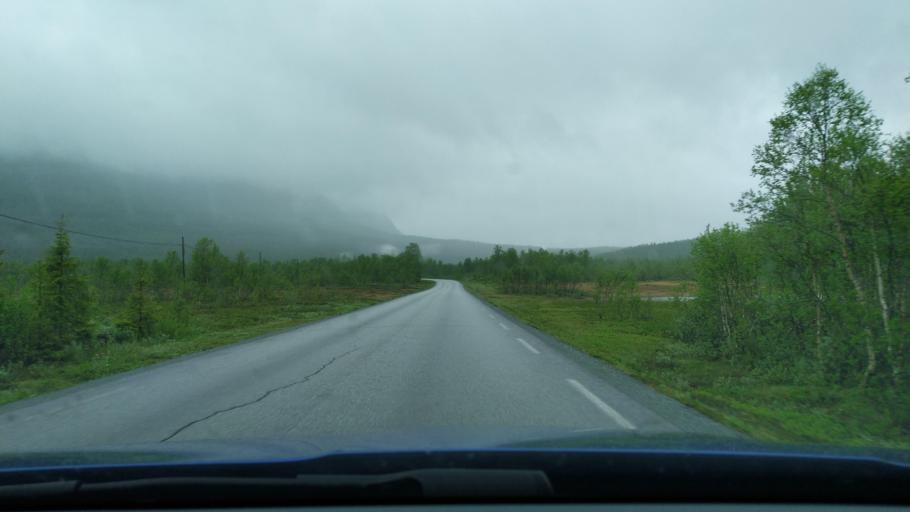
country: NO
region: Troms
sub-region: Dyroy
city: Brostadbotn
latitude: 69.0305
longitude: 17.7385
